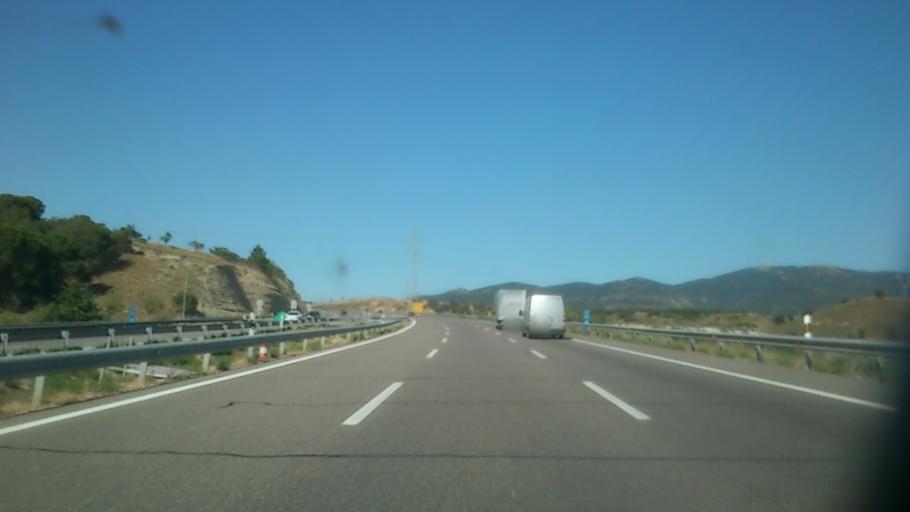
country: ES
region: Aragon
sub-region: Provincia de Zaragoza
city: Villalba de Perejil
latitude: 41.3645
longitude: -1.5850
